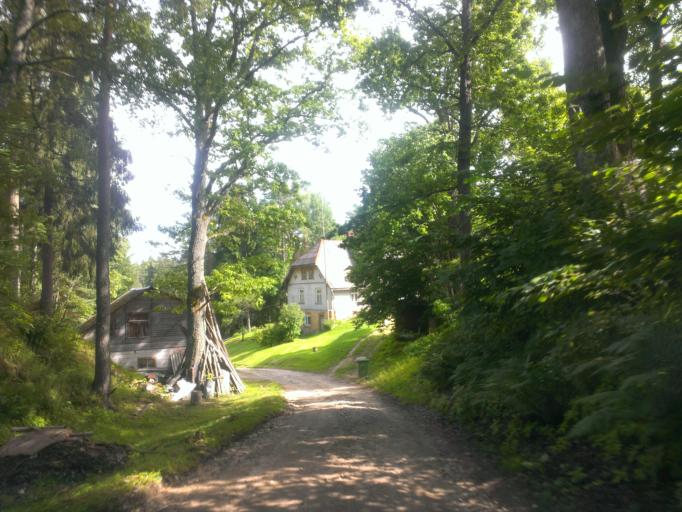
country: LV
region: Ligatne
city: Ligatne
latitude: 57.2340
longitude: 25.0331
